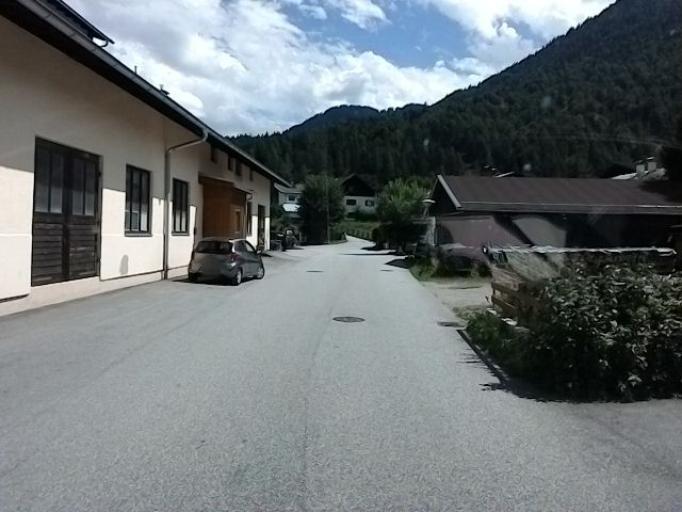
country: AT
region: Tyrol
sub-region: Politischer Bezirk Innsbruck Land
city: Scharnitz
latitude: 47.3863
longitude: 11.2655
